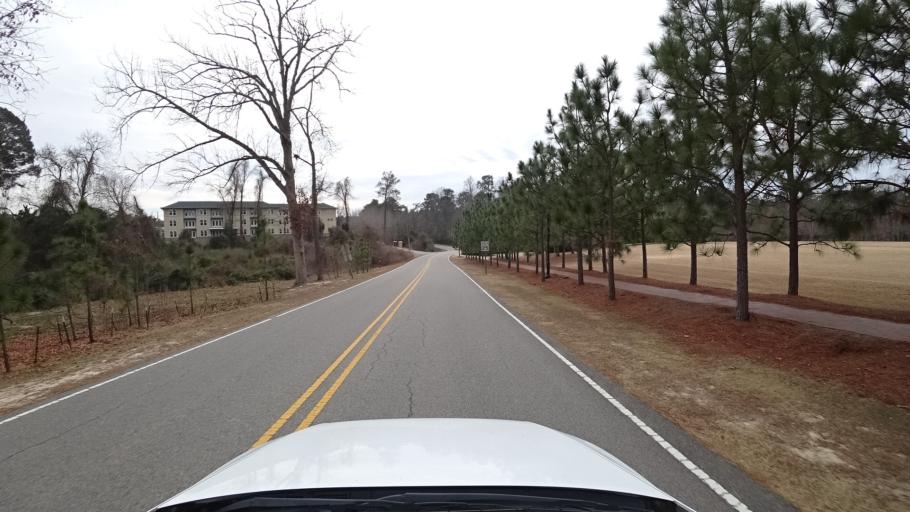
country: US
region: North Carolina
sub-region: Moore County
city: Pinehurst
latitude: 35.2030
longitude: -79.4701
